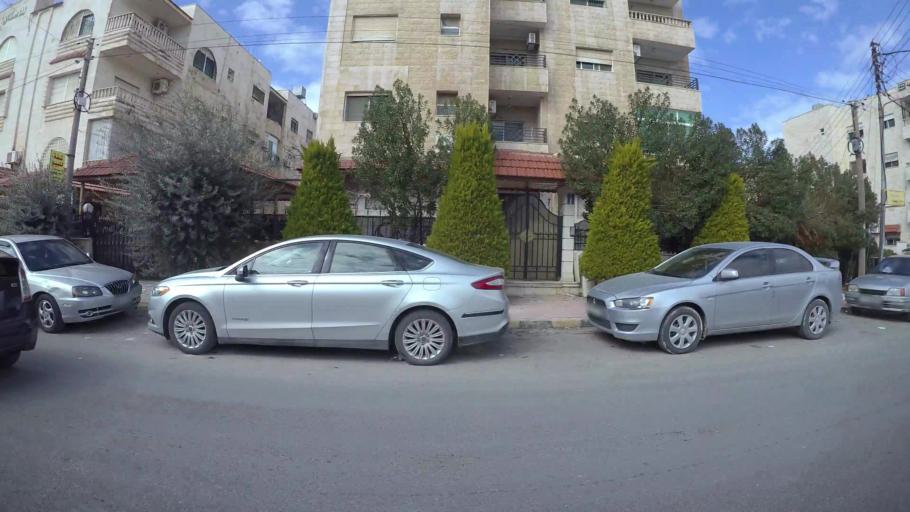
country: JO
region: Amman
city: Al Jubayhah
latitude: 31.9986
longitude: 35.8407
